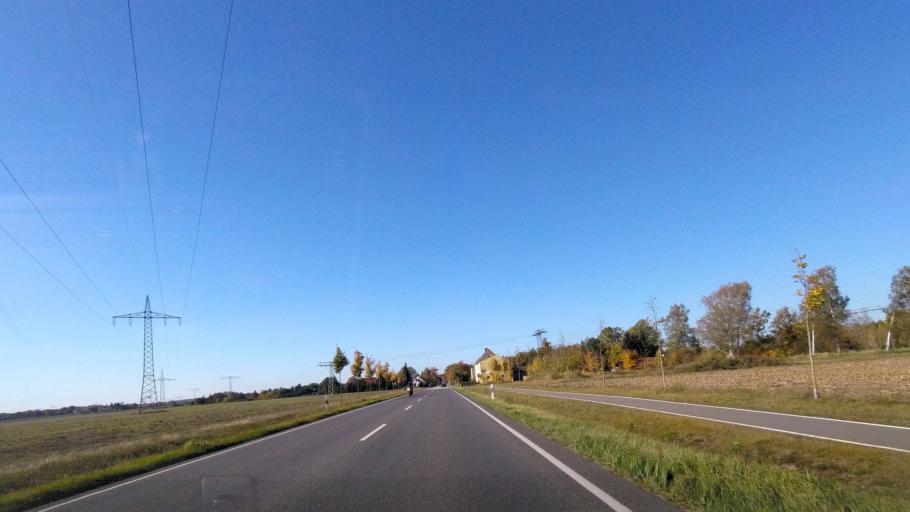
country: DE
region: Saxony-Anhalt
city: Muhlanger
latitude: 51.8502
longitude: 12.7575
